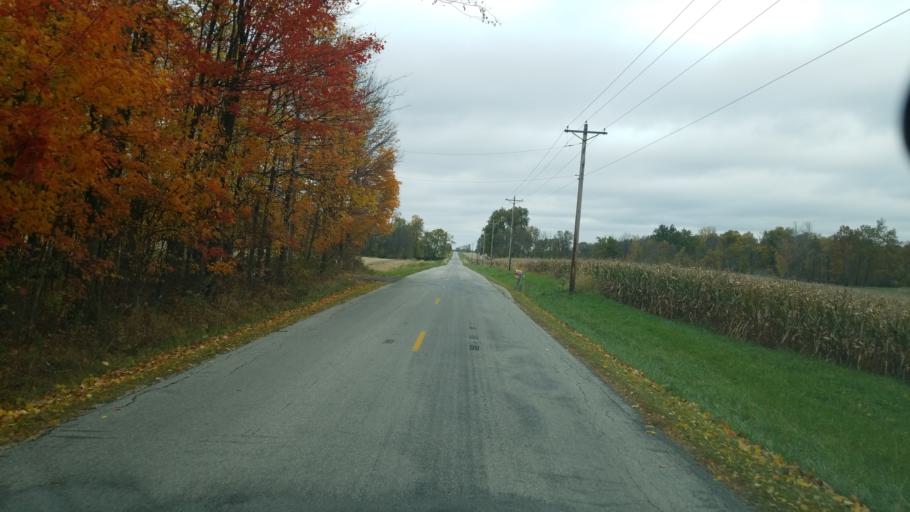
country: US
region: Ohio
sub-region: Sandusky County
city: Mount Carmel
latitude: 41.0690
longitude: -82.9575
